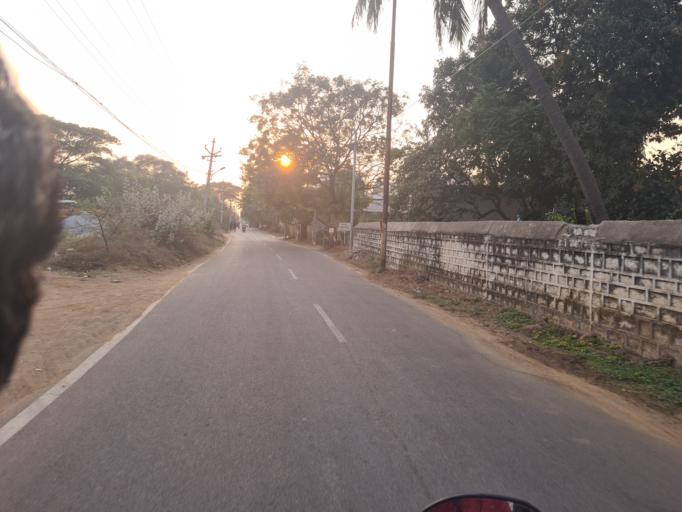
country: IN
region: Telangana
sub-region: Medak
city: Serilingampalle
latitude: 17.4810
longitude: 78.3041
